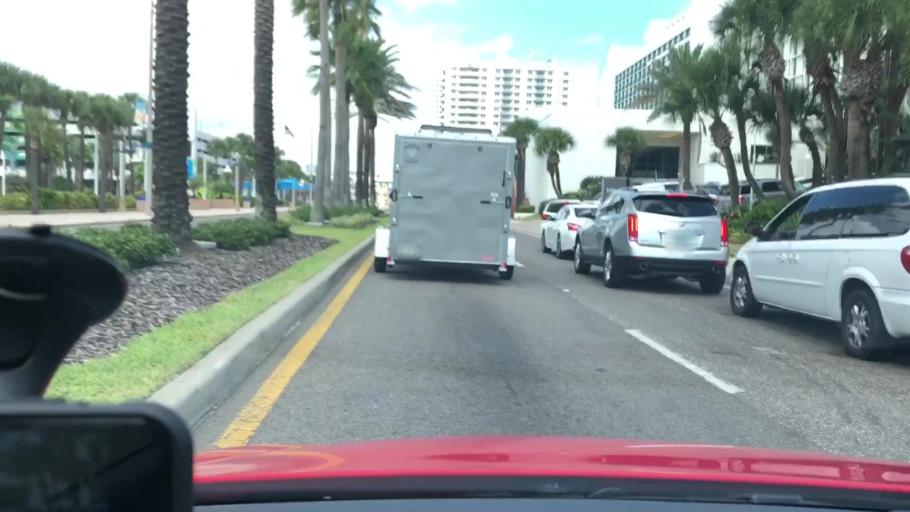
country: US
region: Florida
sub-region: Volusia County
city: Daytona Beach
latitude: 29.2285
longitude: -81.0090
